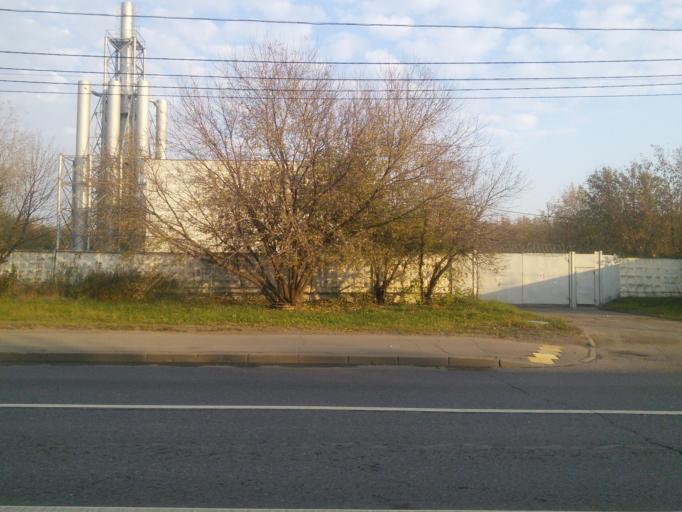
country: RU
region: Moskovskaya
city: Fili
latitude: 55.7591
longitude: 37.4653
